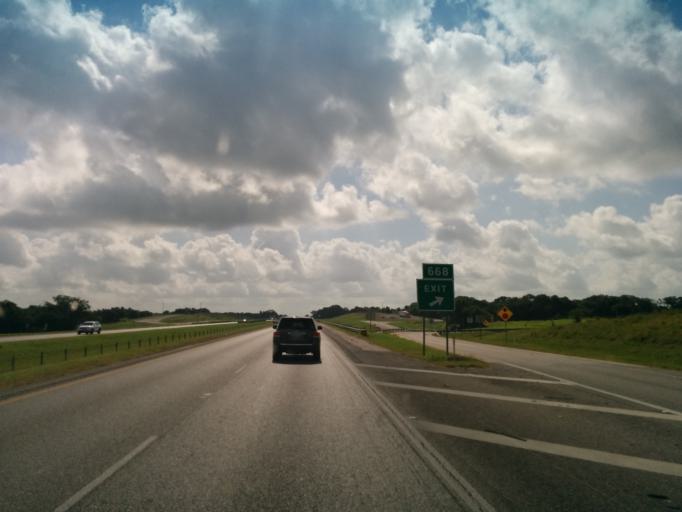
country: US
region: Texas
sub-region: Fayette County
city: Flatonia
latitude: 29.6914
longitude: -97.0058
